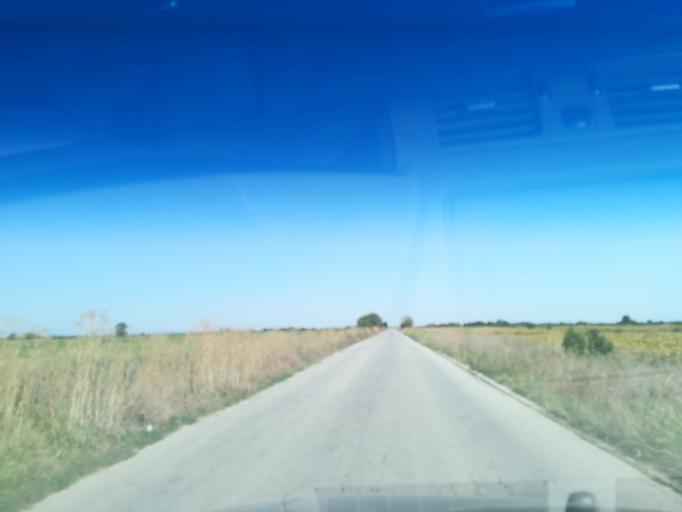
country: BG
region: Plovdiv
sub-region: Obshtina Suedinenie
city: Suedinenie
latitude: 42.2511
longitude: 24.4815
